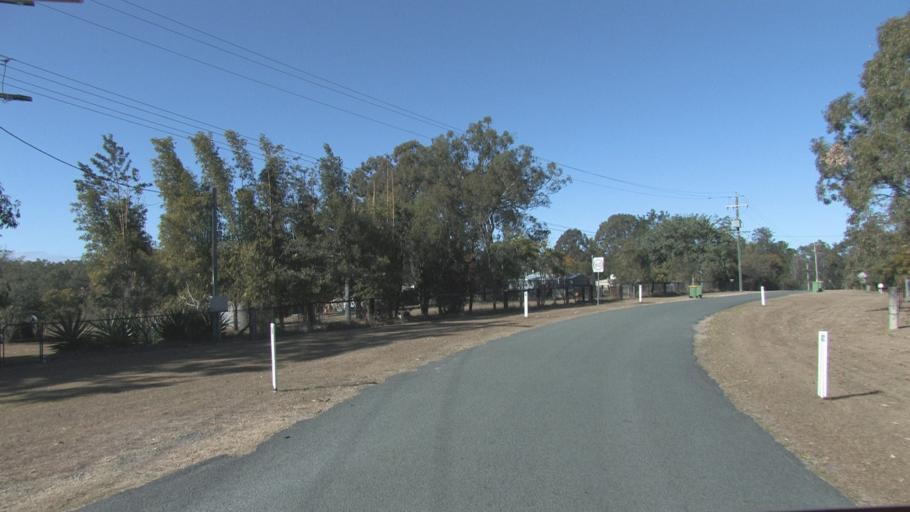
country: AU
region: Queensland
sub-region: Logan
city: North Maclean
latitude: -27.7869
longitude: 153.0063
